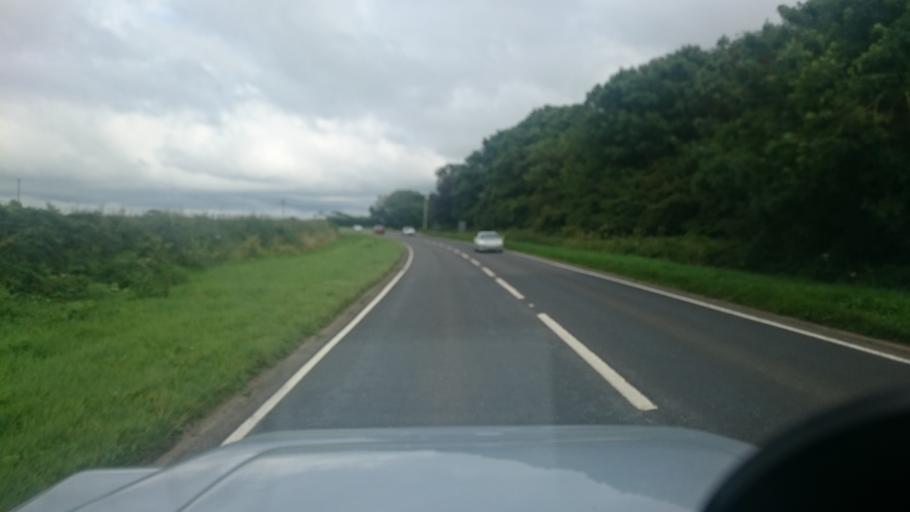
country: GB
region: Wales
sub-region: Pembrokeshire
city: Wiston
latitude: 51.8009
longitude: -4.8495
